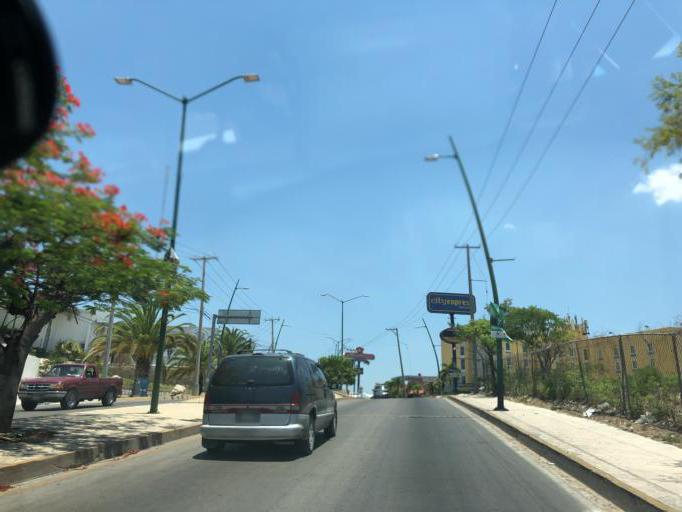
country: MX
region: Chiapas
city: Tuxtla Gutierrez
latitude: 16.7475
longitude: -93.1428
